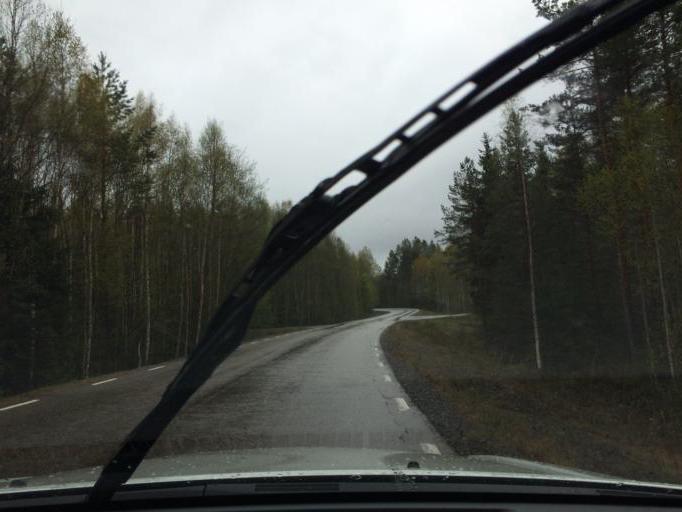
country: SE
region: Dalarna
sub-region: Ludvika Kommun
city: Grangesberg
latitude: 60.0391
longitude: 14.9097
